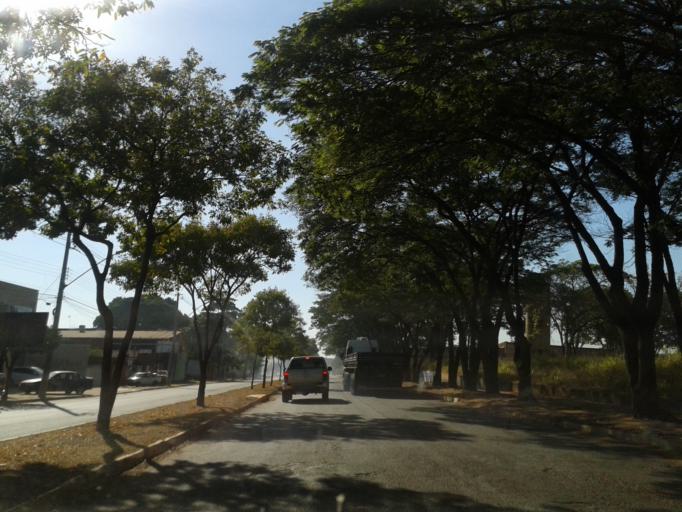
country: BR
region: Goias
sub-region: Goiania
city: Goiania
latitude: -16.6523
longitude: -49.3371
